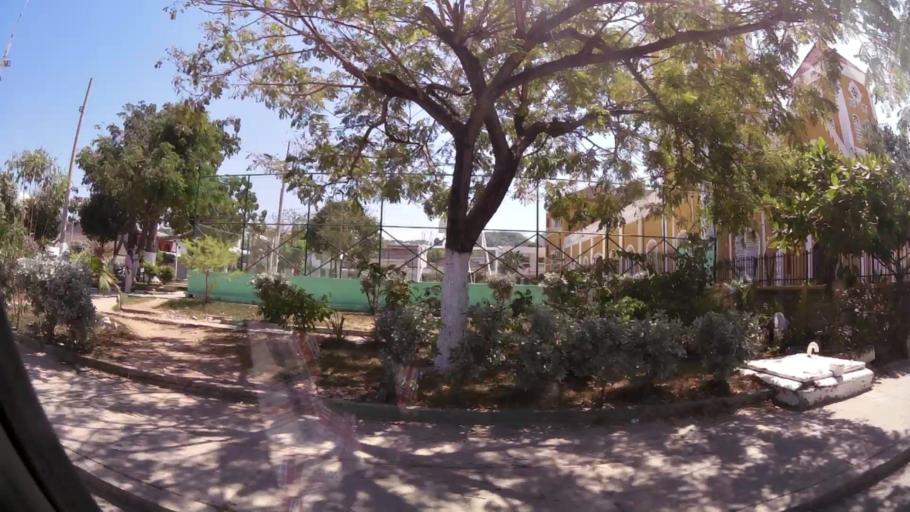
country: CO
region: Bolivar
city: Cartagena
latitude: 10.4309
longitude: -75.5342
